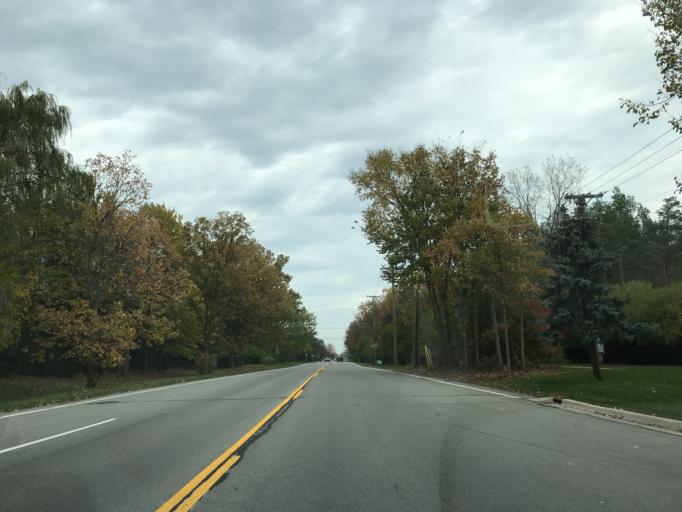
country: US
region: Michigan
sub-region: Oakland County
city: Franklin
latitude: 42.4768
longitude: -83.3185
